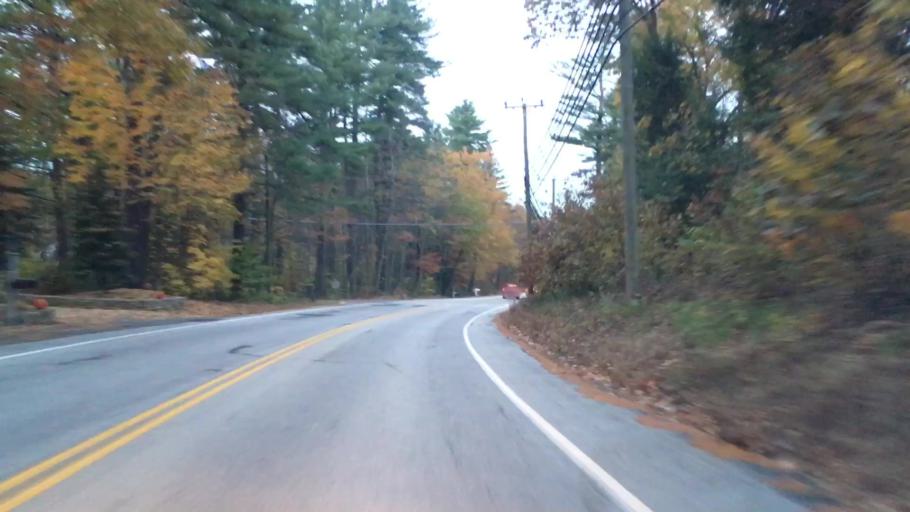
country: US
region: New Hampshire
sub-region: Hillsborough County
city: Milford
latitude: 42.8580
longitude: -71.6346
